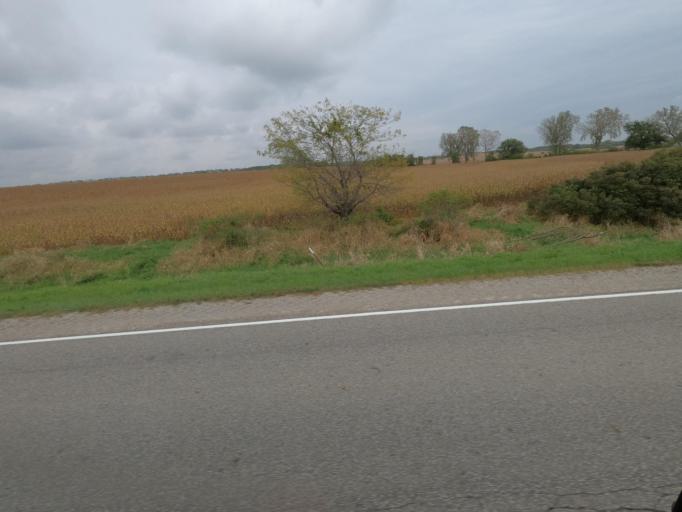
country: US
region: Iowa
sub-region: Wapello County
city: Ottumwa
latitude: 40.9031
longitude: -92.1986
